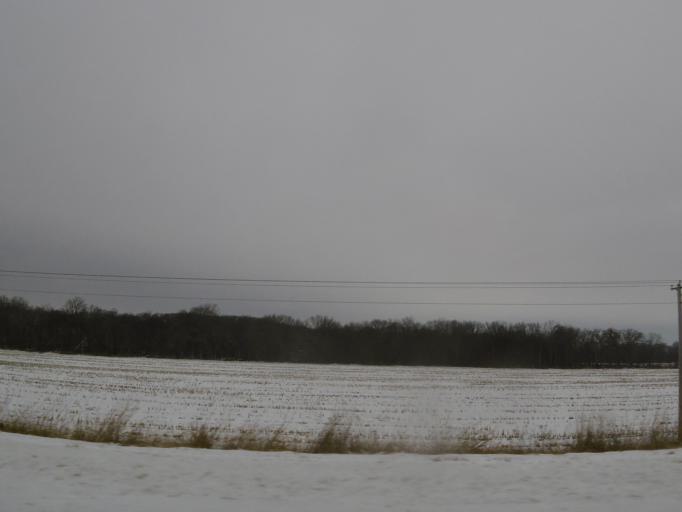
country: US
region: Illinois
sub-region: Hancock County
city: Nauvoo
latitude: 40.5781
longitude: -91.5654
